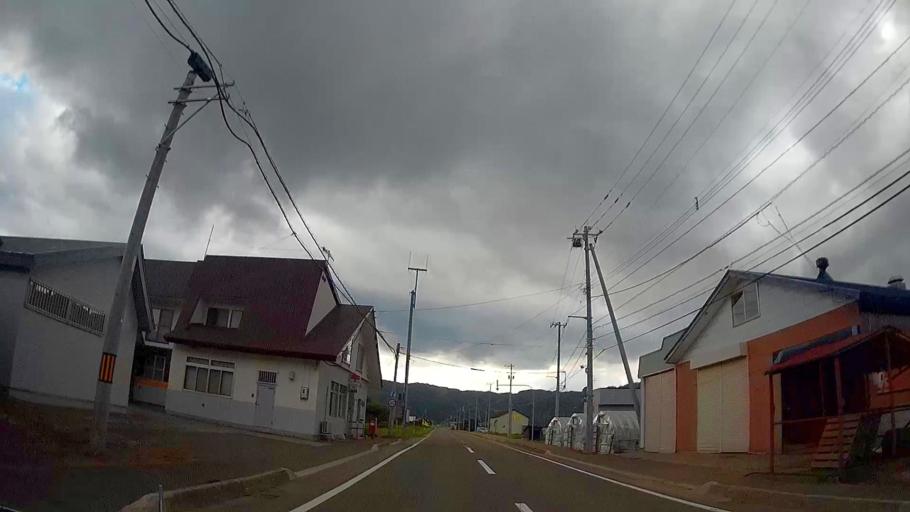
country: JP
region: Hokkaido
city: Nanae
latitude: 42.1215
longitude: 140.4440
